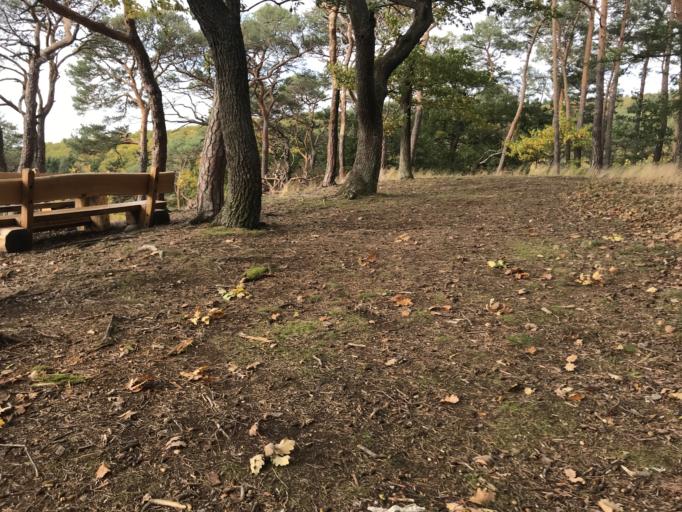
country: DE
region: Rheinland-Pfalz
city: Kirchheimbolanden
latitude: 49.6544
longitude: 7.9880
